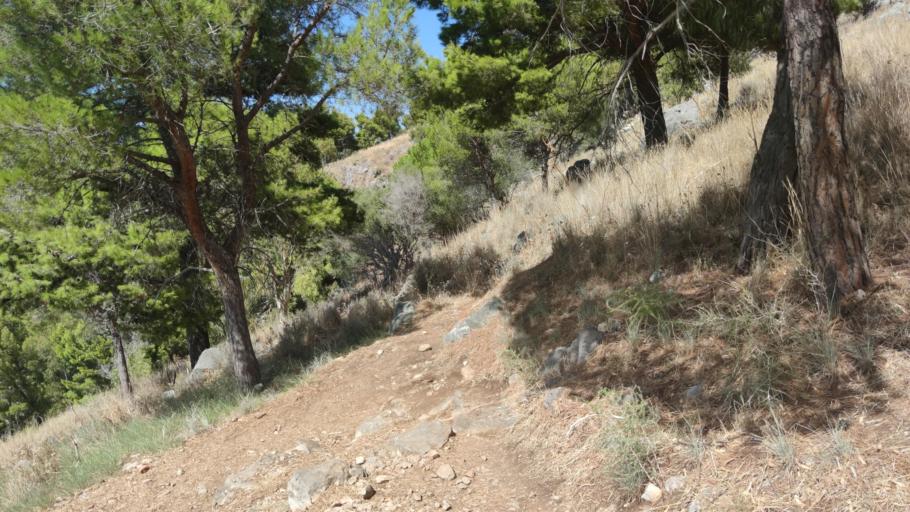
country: IT
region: Sicily
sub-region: Palermo
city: Cefalu
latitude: 38.0365
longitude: 14.0251
